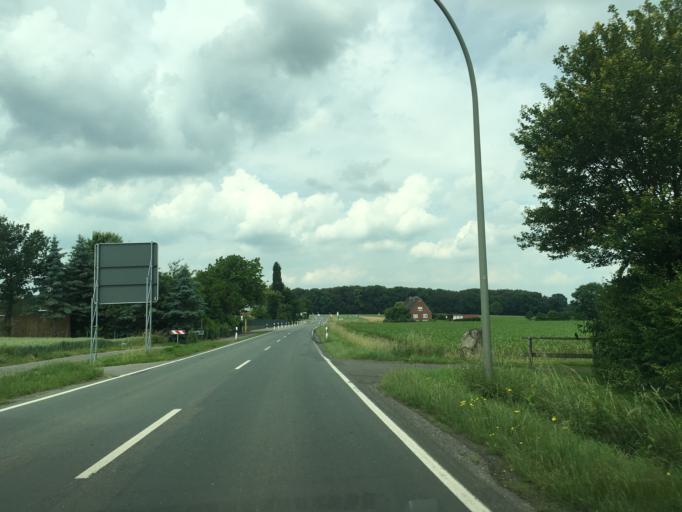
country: DE
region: North Rhine-Westphalia
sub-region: Regierungsbezirk Munster
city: Havixbeck
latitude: 51.9780
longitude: 7.4037
